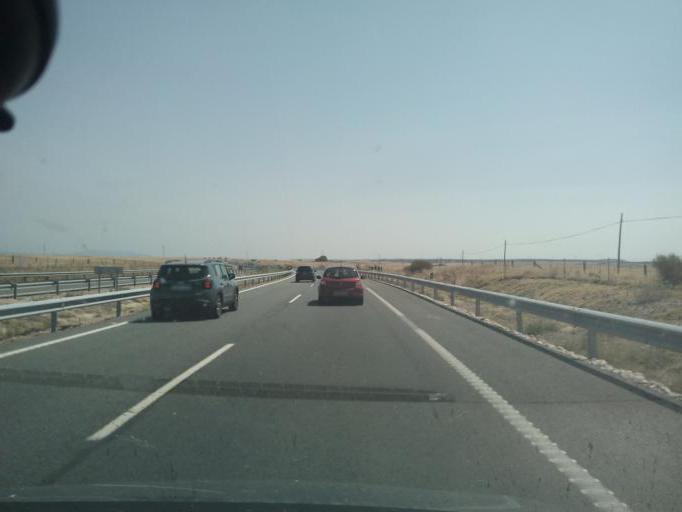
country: ES
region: Extremadura
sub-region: Provincia de Caceres
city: Berrocalejo
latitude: 39.8928
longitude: -5.3705
